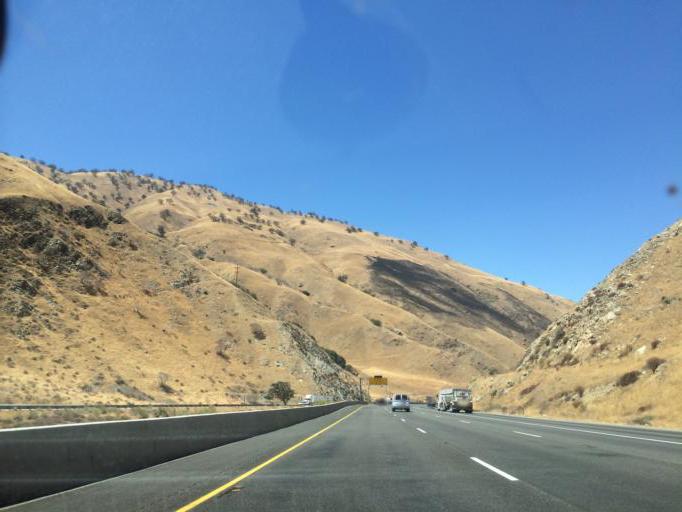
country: US
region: California
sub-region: Kern County
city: Lebec
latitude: 34.8942
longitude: -118.9176
